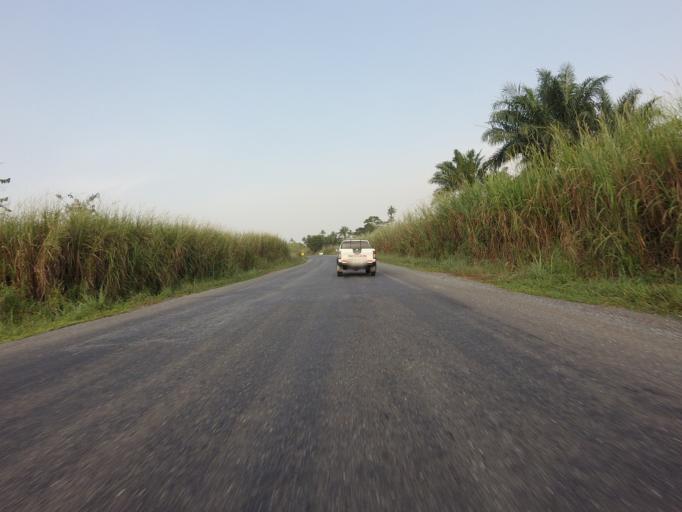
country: GH
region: Volta
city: Ho
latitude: 6.4603
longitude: 0.2190
